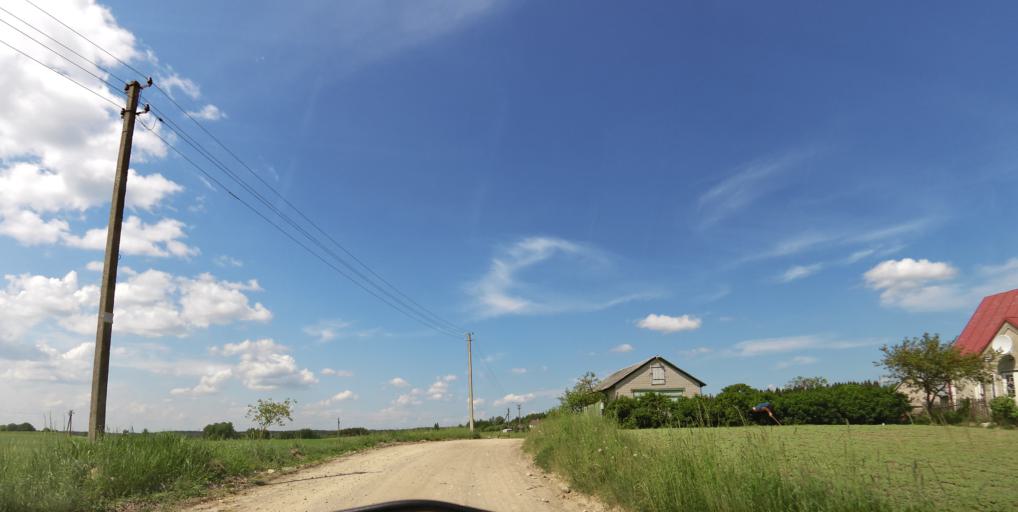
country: LT
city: Grigiskes
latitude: 54.7476
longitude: 25.1094
